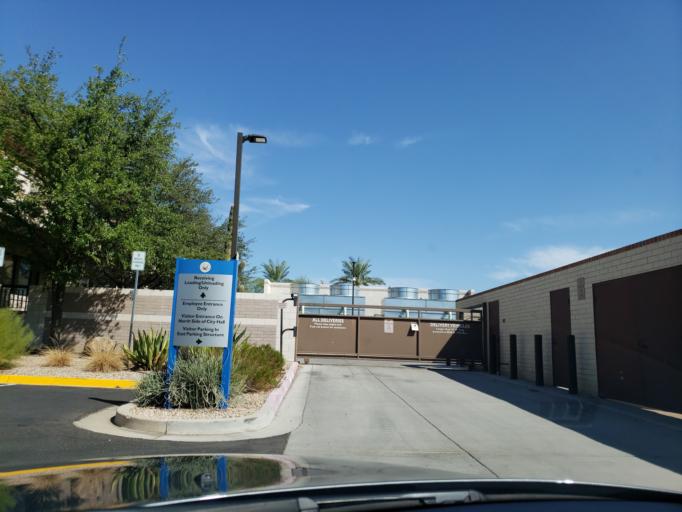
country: US
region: Arizona
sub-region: Maricopa County
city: Peoria
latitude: 33.5758
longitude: -112.2393
